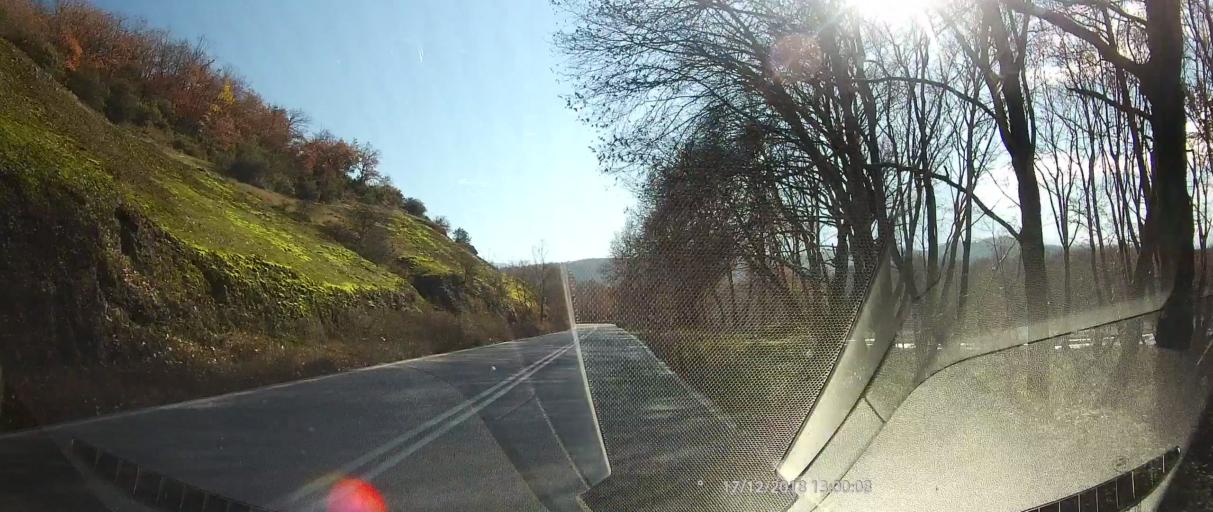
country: GR
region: Thessaly
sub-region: Trikala
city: Kastraki
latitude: 39.7309
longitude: 21.5644
